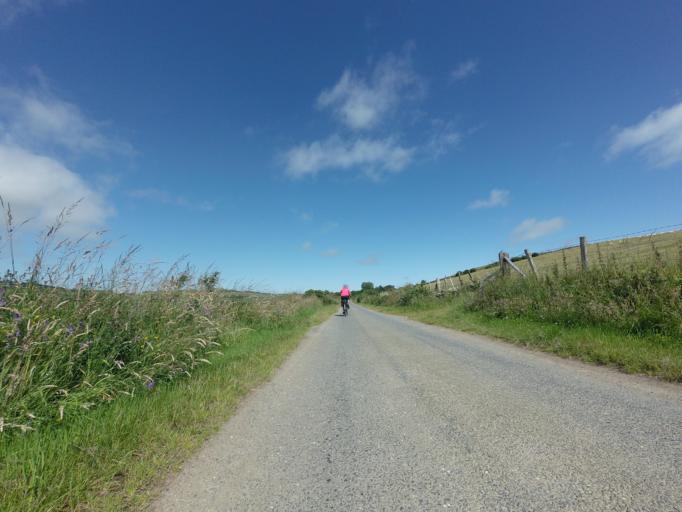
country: GB
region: Scotland
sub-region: Aberdeenshire
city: Banff
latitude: 57.6018
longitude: -2.5121
